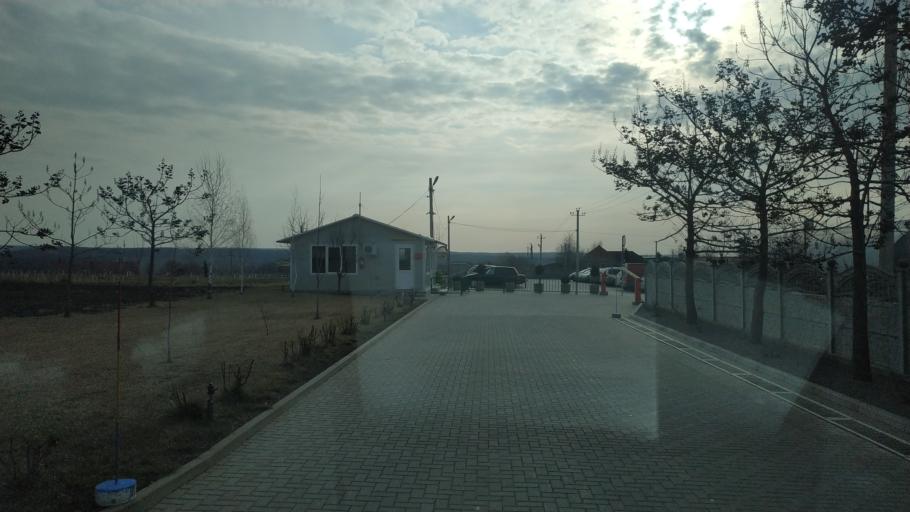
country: MD
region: Chisinau
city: Singera
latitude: 46.9701
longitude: 29.0631
